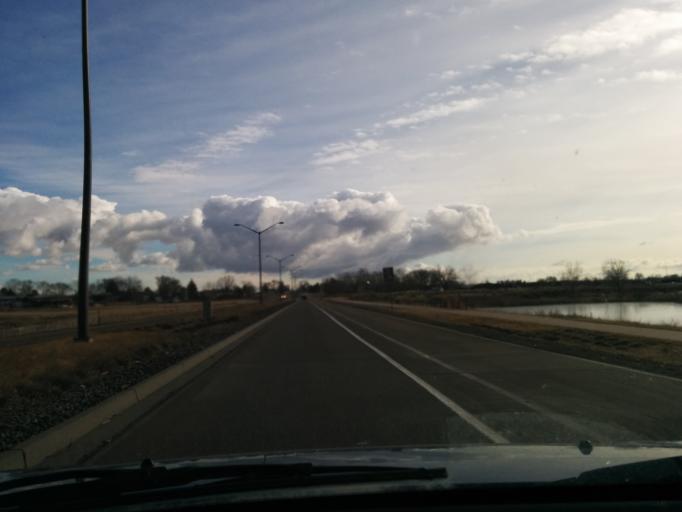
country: US
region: Colorado
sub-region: Larimer County
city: Fort Collins
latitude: 40.5668
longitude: -105.0194
